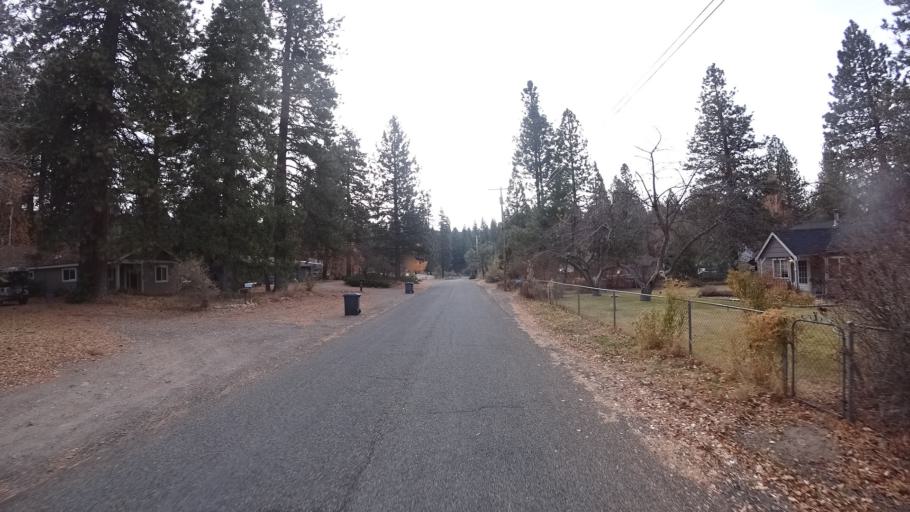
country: US
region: California
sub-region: Siskiyou County
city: Weed
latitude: 41.4468
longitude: -122.3589
